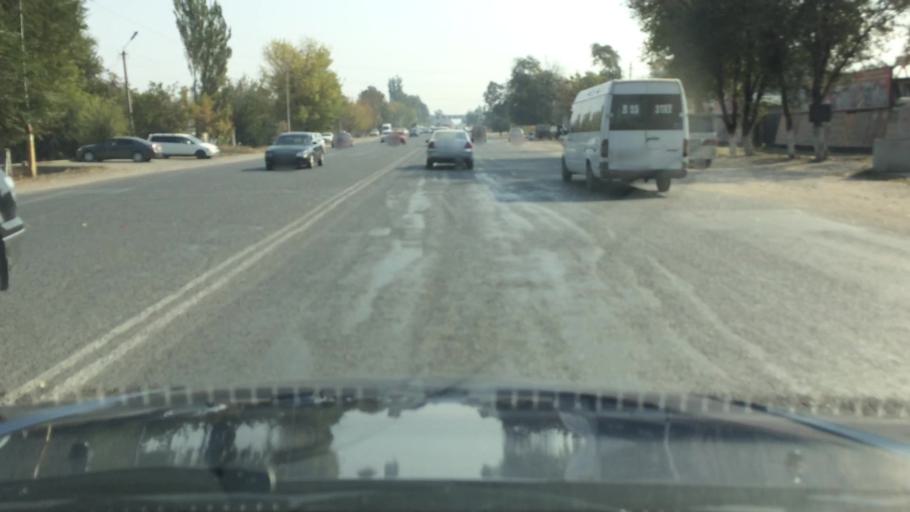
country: KG
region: Chuy
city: Lebedinovka
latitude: 42.8863
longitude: 74.6752
